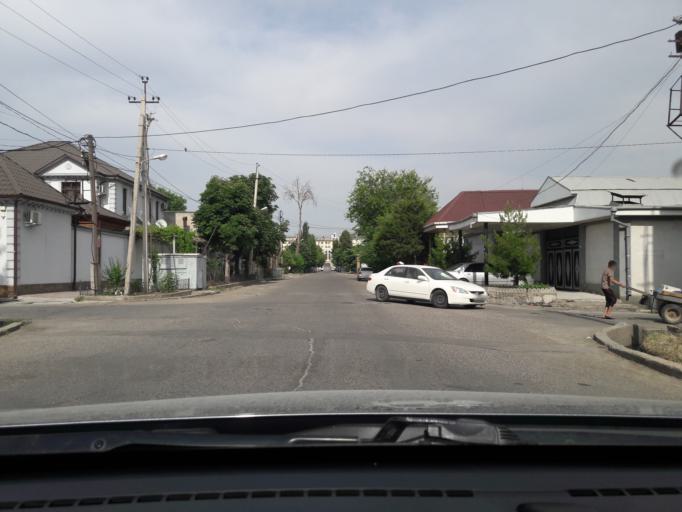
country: TJ
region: Dushanbe
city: Dushanbe
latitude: 38.5381
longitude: 68.7575
